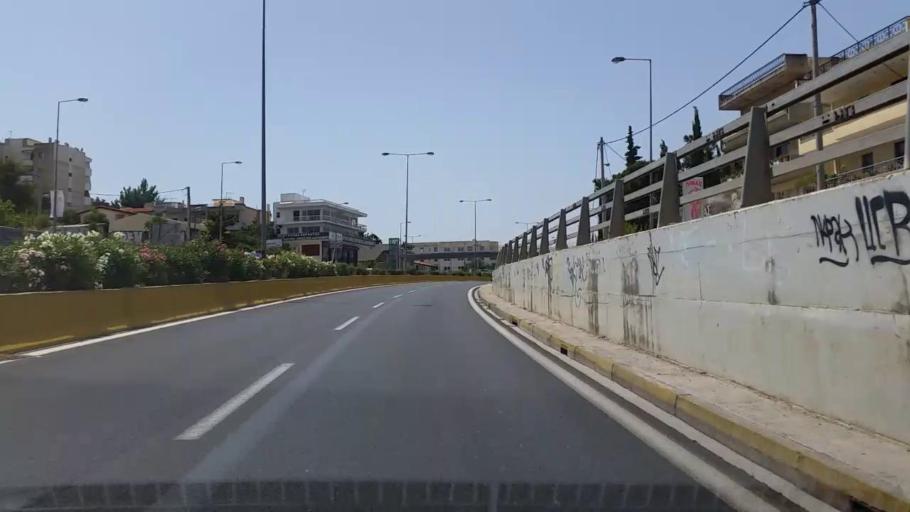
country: GR
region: Attica
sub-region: Nomarchia Athinas
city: Agia Paraskevi
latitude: 38.0109
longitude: 23.8408
